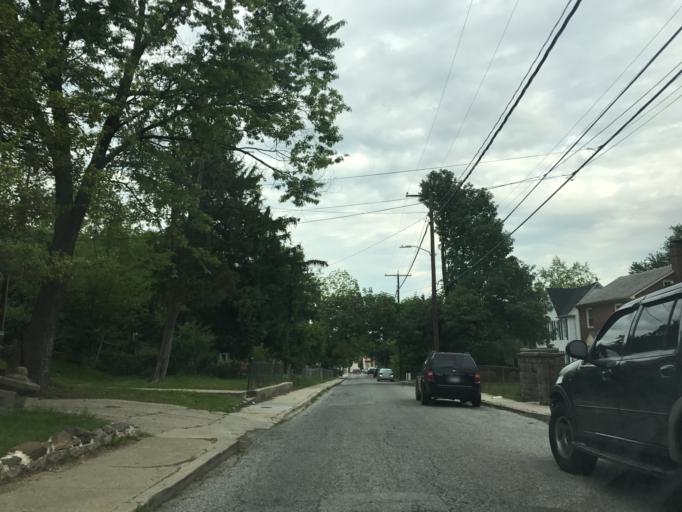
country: US
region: Maryland
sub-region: Baltimore County
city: Parkville
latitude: 39.3482
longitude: -76.5683
